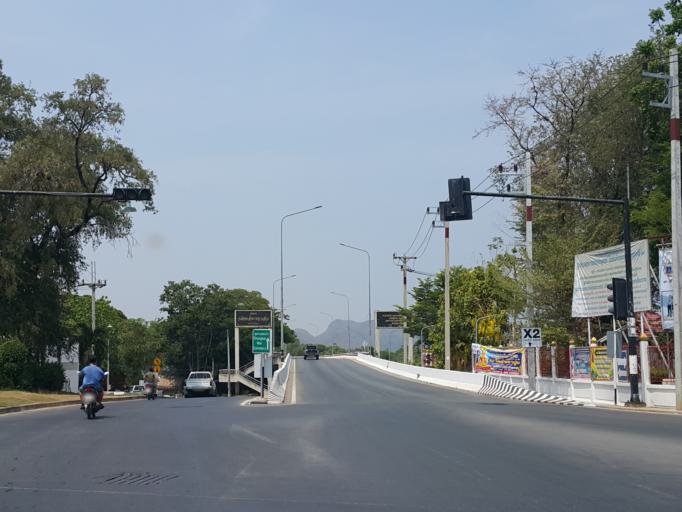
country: TH
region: Kanchanaburi
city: Kanchanaburi
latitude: 14.0261
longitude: 99.5270
